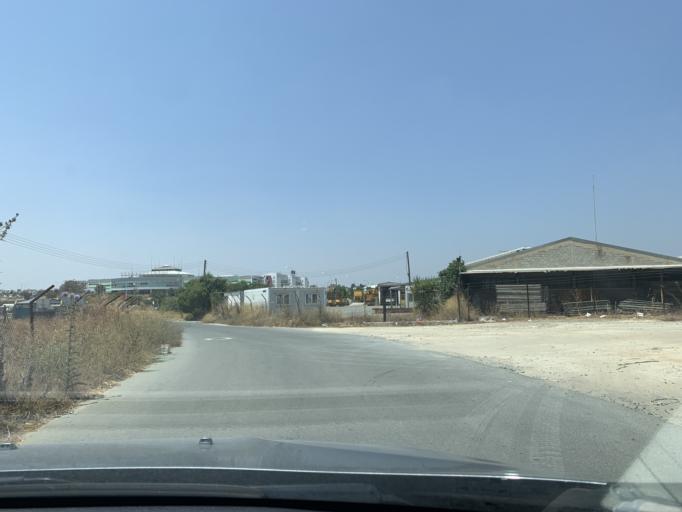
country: CY
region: Lefkosia
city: Nicosia
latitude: 35.1235
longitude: 33.3579
